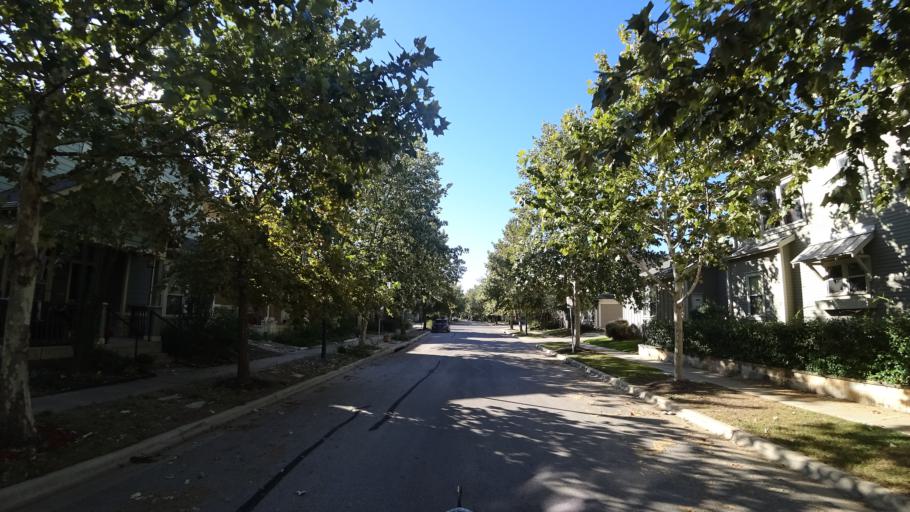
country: US
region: Texas
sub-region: Travis County
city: Austin
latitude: 30.2948
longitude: -97.7011
